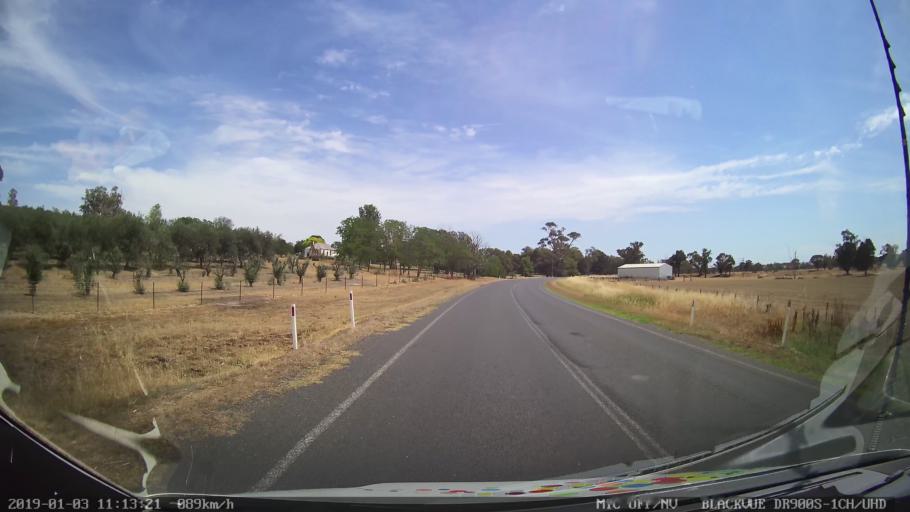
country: AU
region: New South Wales
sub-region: Young
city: Young
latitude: -34.1898
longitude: 148.2606
